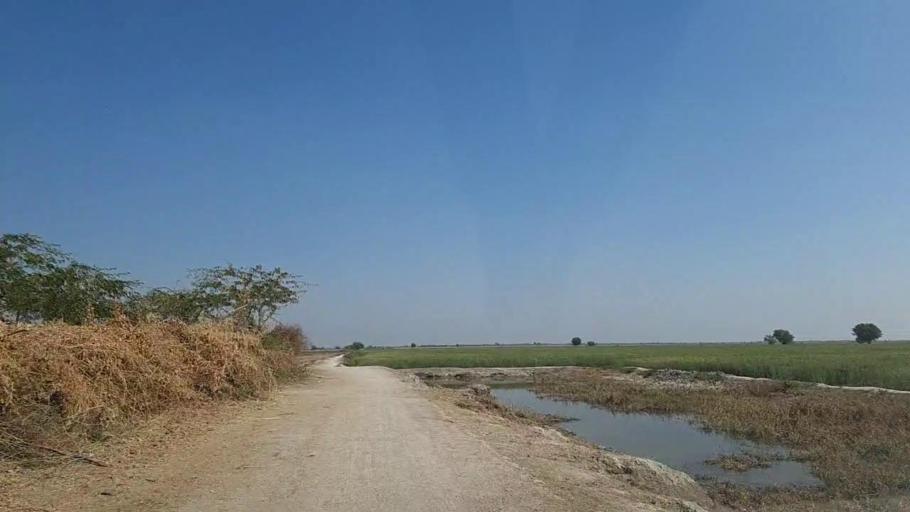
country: PK
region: Sindh
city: Pithoro
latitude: 25.4165
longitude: 69.4179
